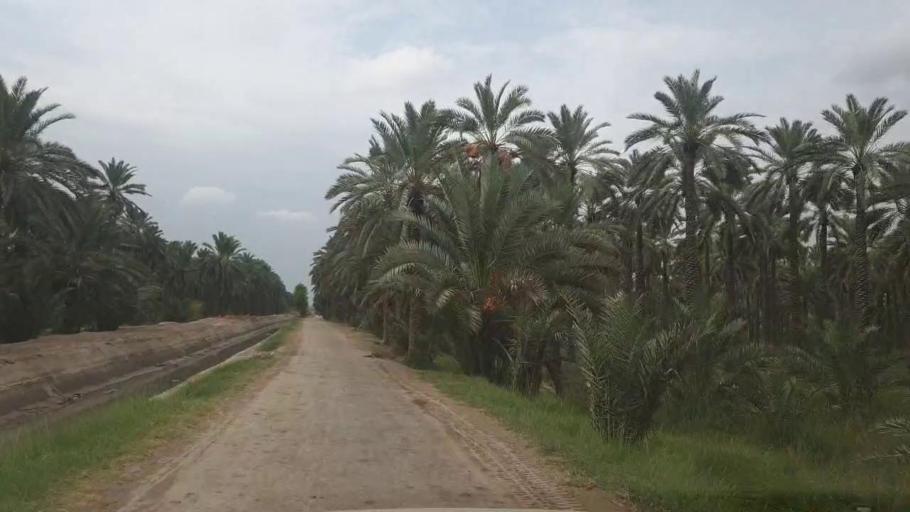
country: PK
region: Sindh
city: Sukkur
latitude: 27.6218
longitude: 68.8068
